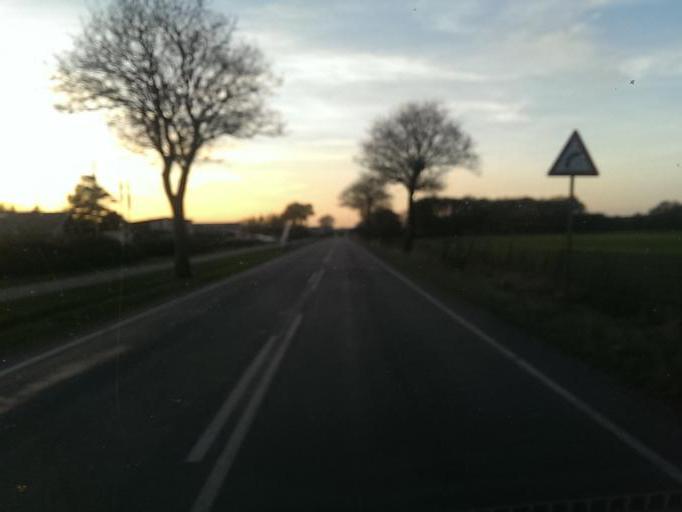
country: DK
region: South Denmark
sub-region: Esbjerg Kommune
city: Bramming
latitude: 55.4691
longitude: 8.6742
